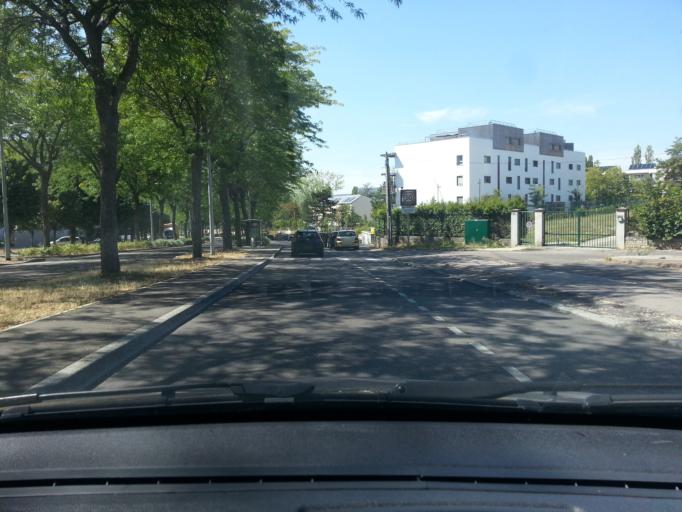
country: FR
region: Bourgogne
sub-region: Departement de la Cote-d'Or
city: Saint-Apollinaire
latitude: 47.3342
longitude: 5.0669
